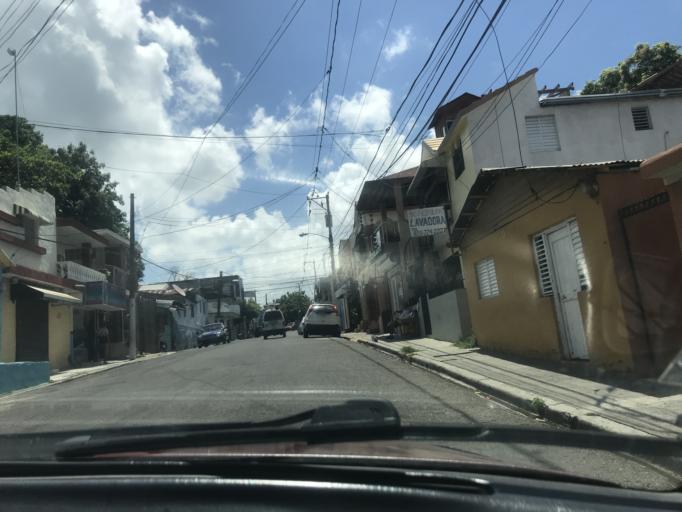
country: DO
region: Santiago
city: Santiago de los Caballeros
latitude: 19.4669
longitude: -70.7022
